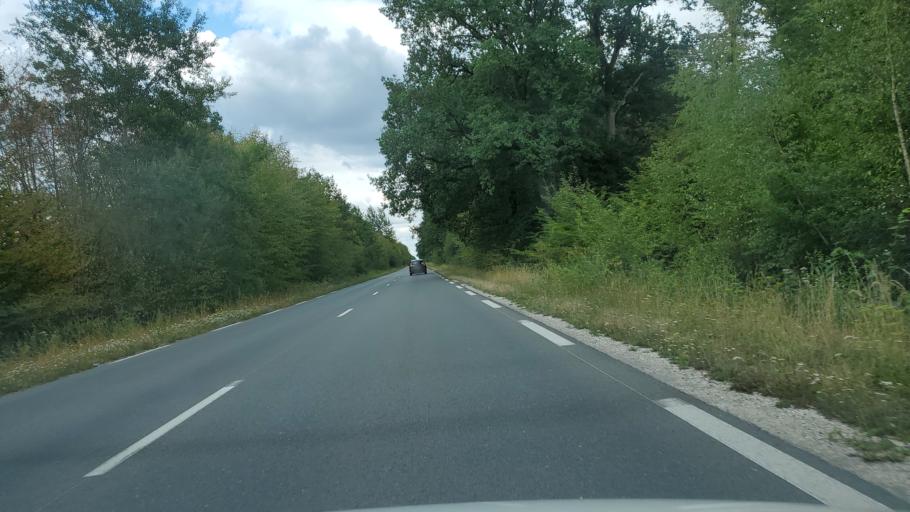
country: FR
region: Ile-de-France
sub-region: Departement de Seine-et-Marne
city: Mortcerf
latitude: 48.7840
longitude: 2.8838
